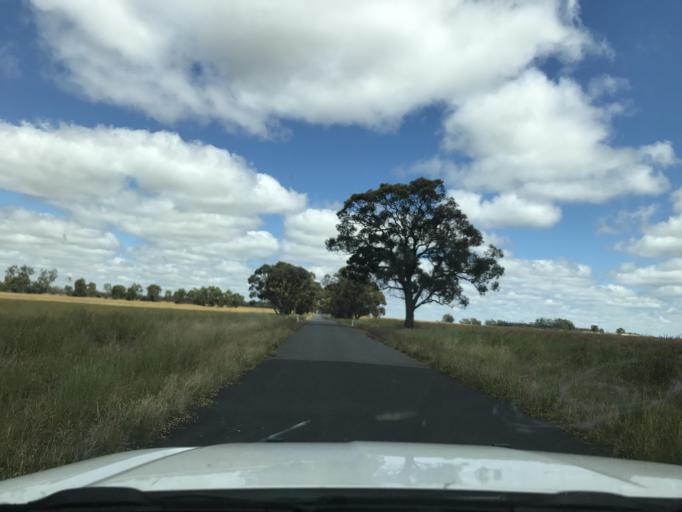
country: AU
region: South Australia
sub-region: Naracoorte and Lucindale
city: Naracoorte
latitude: -36.6838
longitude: 141.3171
